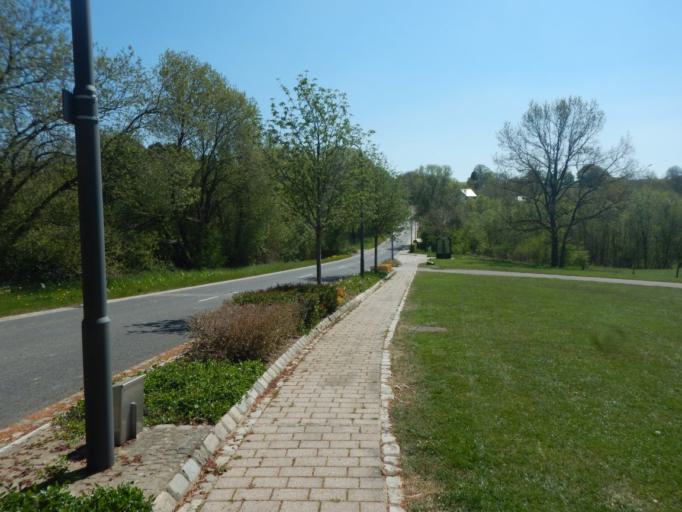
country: LU
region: Diekirch
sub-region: Canton de Clervaux
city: Troisvierges
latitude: 50.1438
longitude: 6.0158
